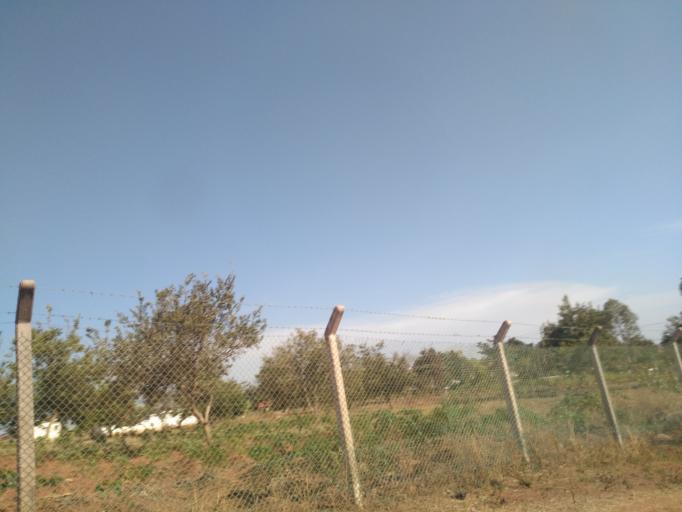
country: TZ
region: Mwanza
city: Mwanza
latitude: -2.4932
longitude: 32.8924
